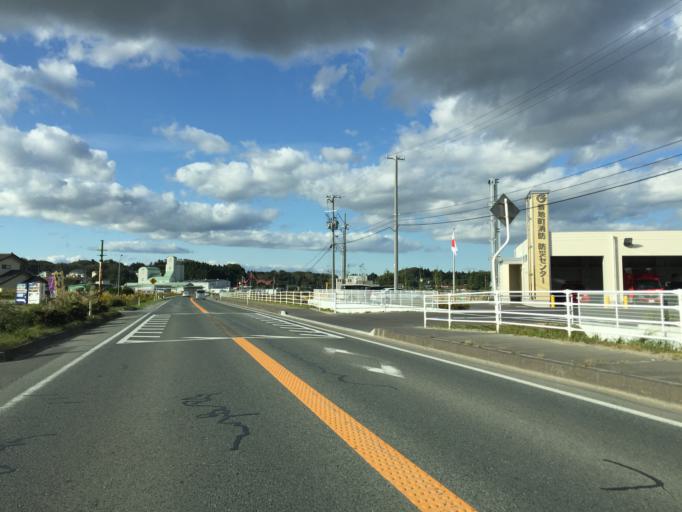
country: JP
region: Miyagi
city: Marumori
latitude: 37.8773
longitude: 140.9172
